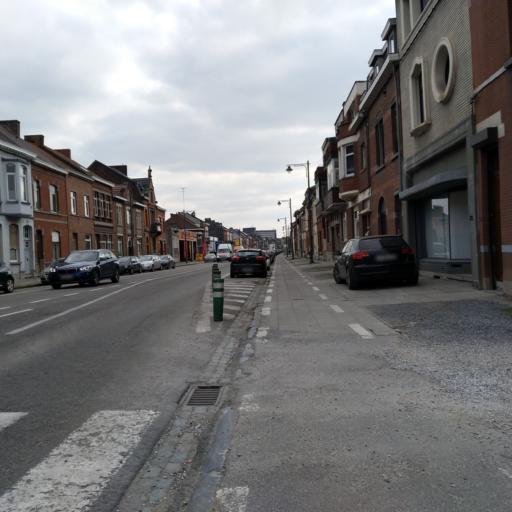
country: BE
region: Wallonia
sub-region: Province du Hainaut
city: Mons
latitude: 50.4687
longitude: 3.9571
